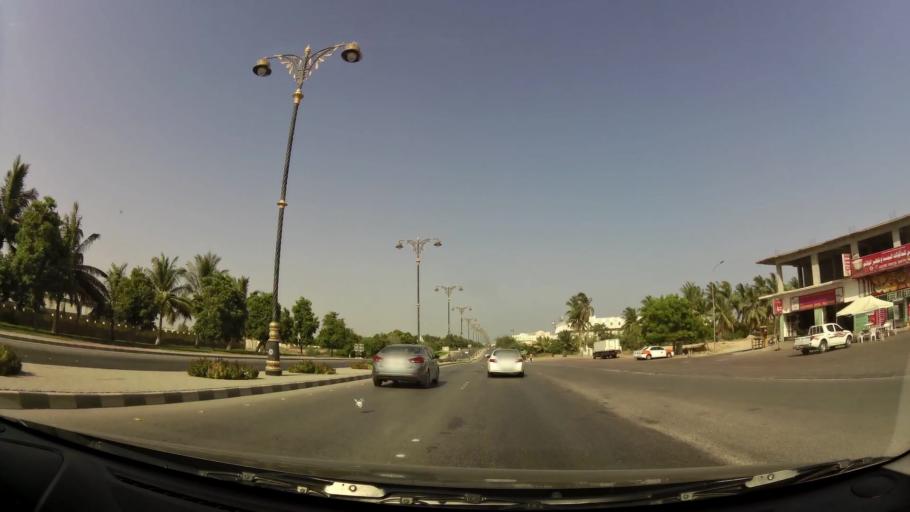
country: OM
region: Zufar
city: Salalah
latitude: 17.0046
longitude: 54.0429
